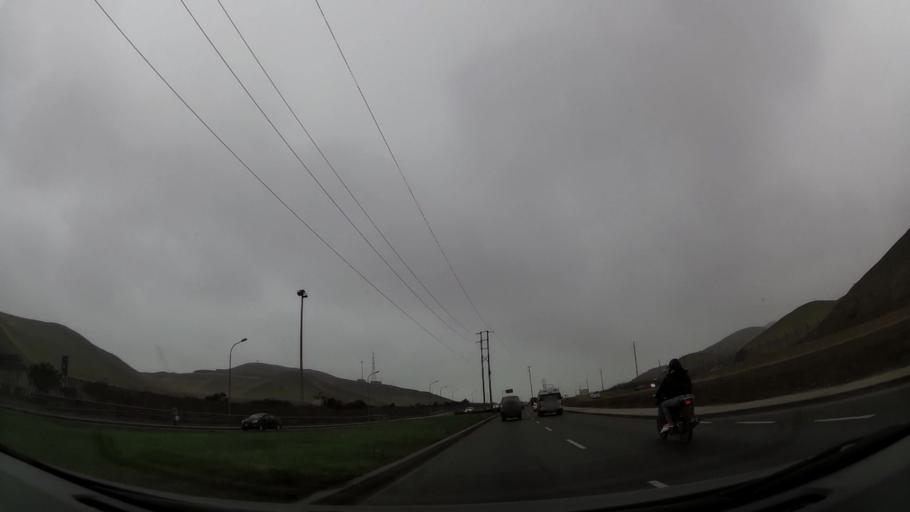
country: PE
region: Lima
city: Ventanilla
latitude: -11.9086
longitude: -77.1286
